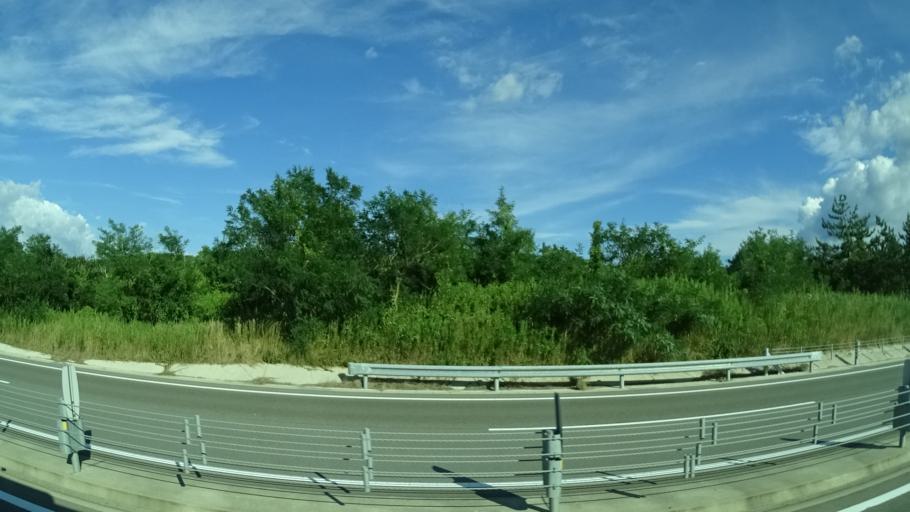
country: JP
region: Ishikawa
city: Tsubata
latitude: 36.6821
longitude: 136.6589
